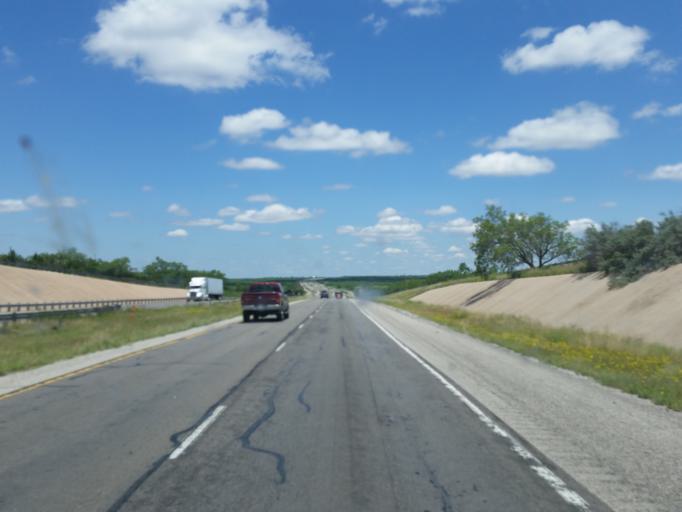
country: US
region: Texas
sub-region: Nolan County
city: Sweetwater
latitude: 32.4941
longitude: -100.3021
